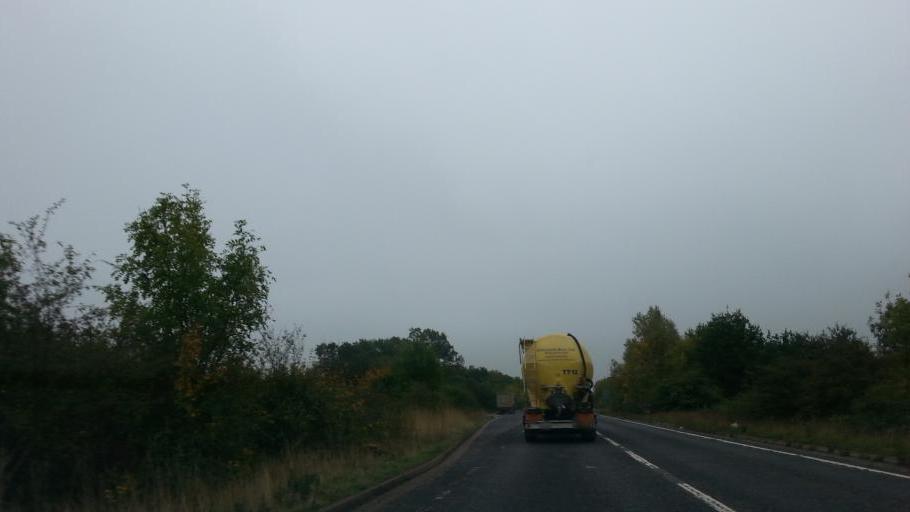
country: GB
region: England
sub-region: Northamptonshire
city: Thrapston
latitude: 52.3847
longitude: -0.5237
